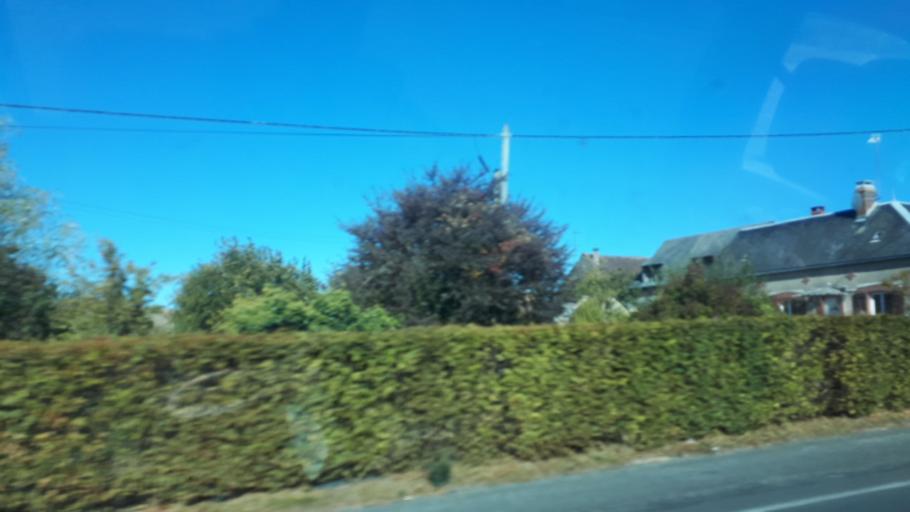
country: FR
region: Centre
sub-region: Departement du Loir-et-Cher
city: Moree
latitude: 47.9386
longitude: 1.2042
